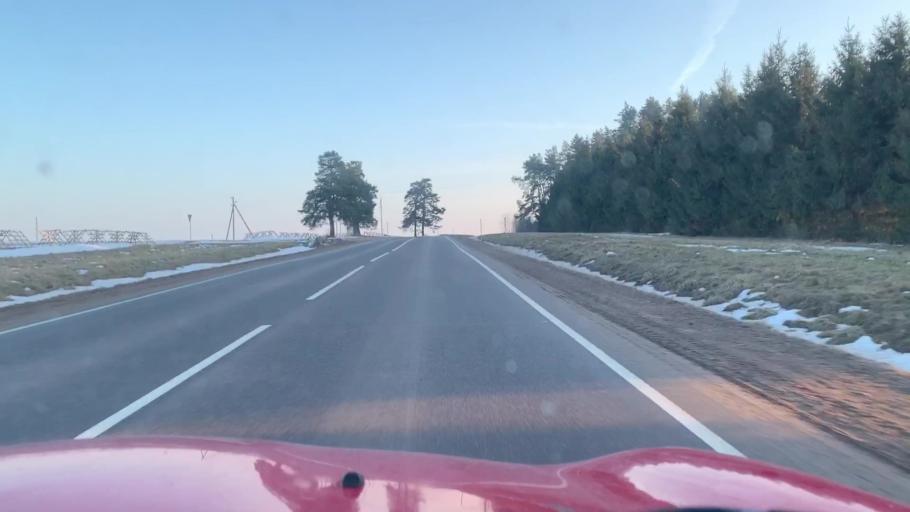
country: BY
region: Grodnenskaya
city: Mir
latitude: 53.4421
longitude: 26.4773
